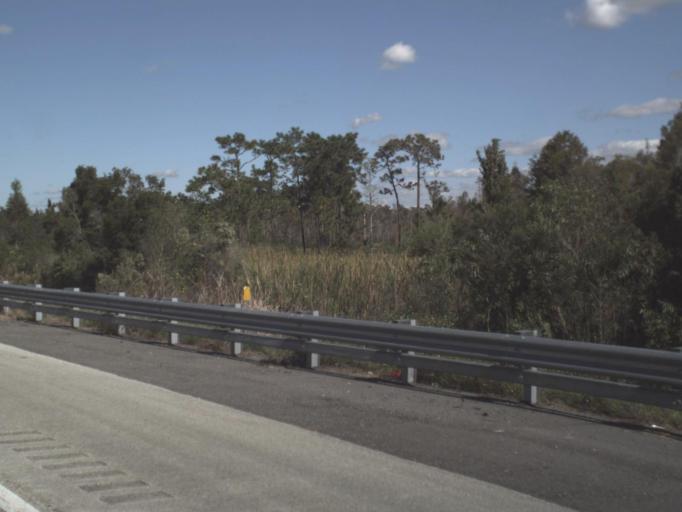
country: US
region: Florida
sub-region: Osceola County
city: Saint Cloud
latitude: 27.9291
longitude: -81.0647
